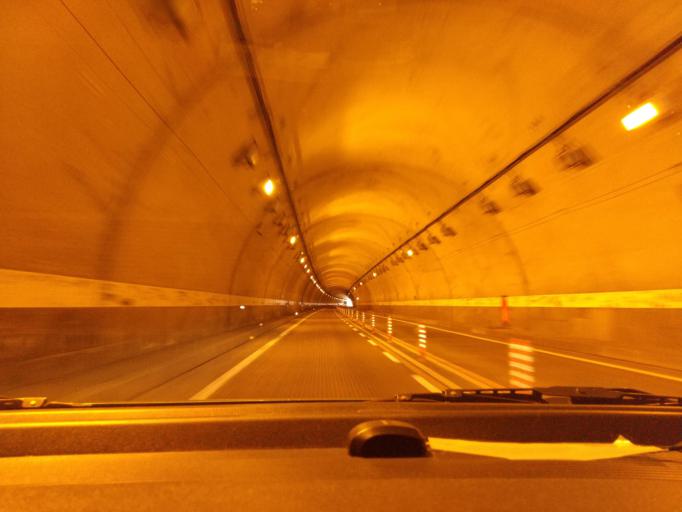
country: JP
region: Akita
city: Yokotemachi
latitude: 39.3160
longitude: 140.7615
